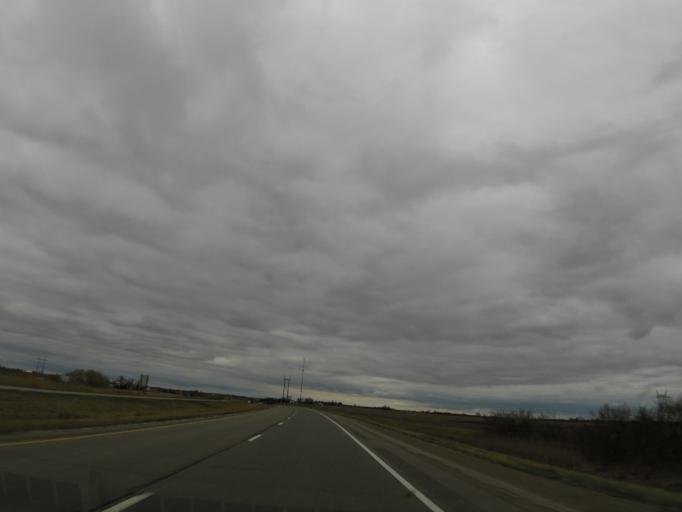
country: US
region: Iowa
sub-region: Washington County
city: Washington
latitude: 41.3198
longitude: -91.5505
